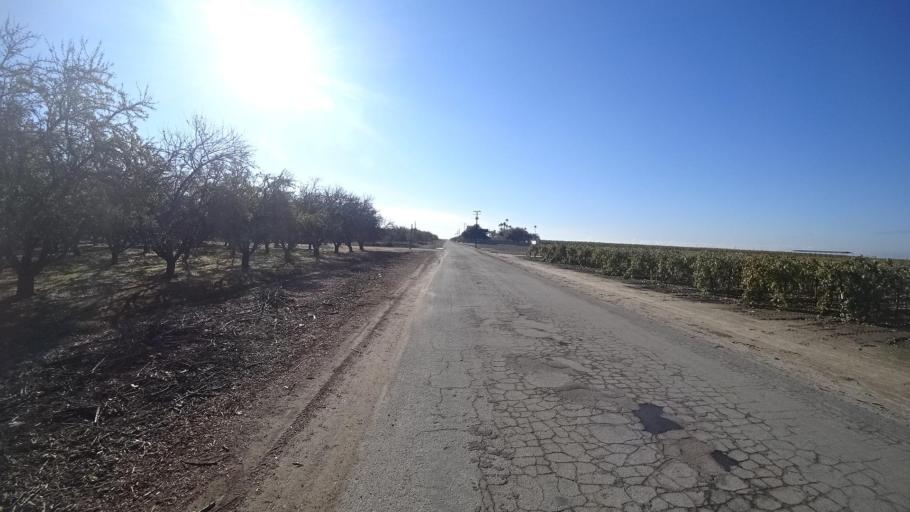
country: US
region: California
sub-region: Kern County
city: McFarland
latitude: 35.6857
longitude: -119.2675
